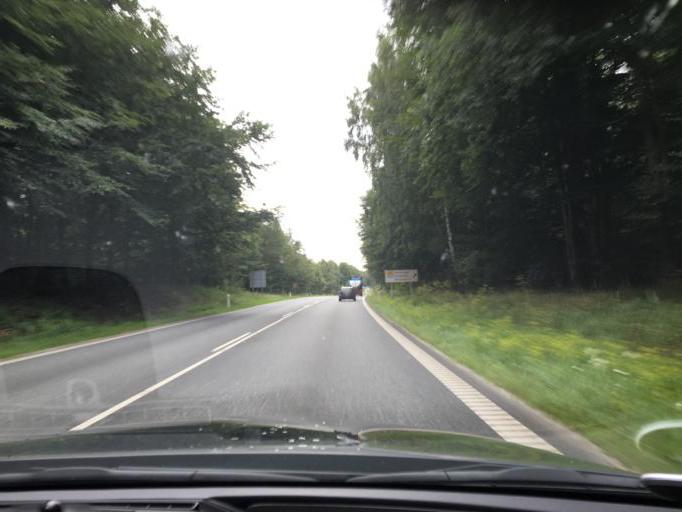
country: DK
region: Capital Region
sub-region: Hillerod Kommune
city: Nodebo
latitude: 55.9495
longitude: 12.3293
